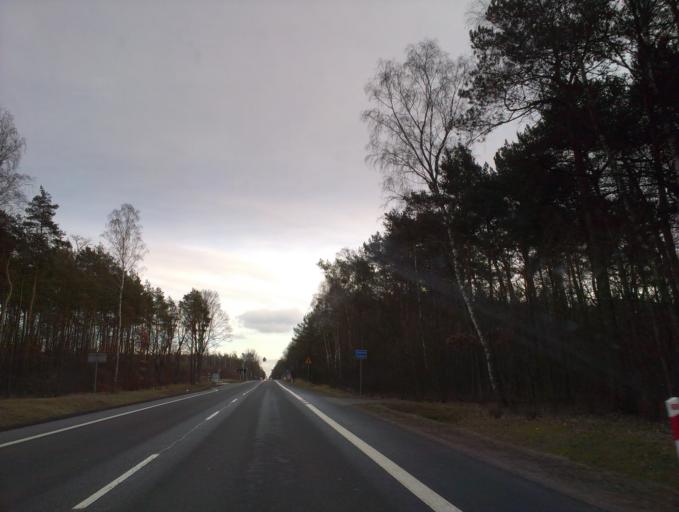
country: PL
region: Masovian Voivodeship
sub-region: Powiat sierpecki
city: Szczutowo
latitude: 52.8837
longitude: 19.5863
